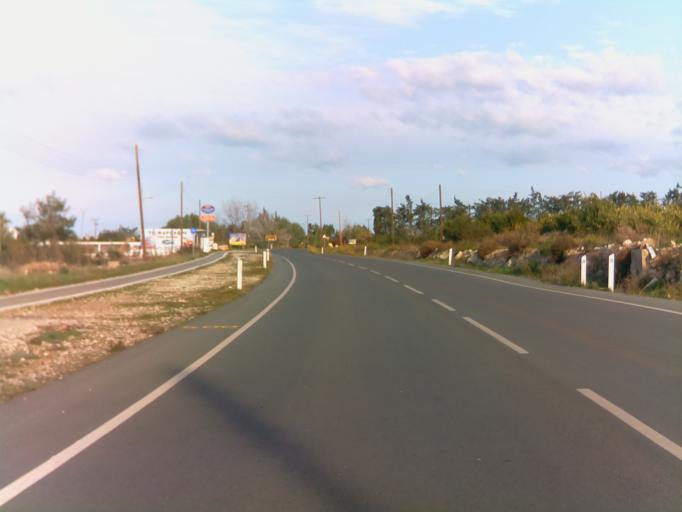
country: CY
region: Pafos
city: Pegeia
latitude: 34.8895
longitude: 32.3379
